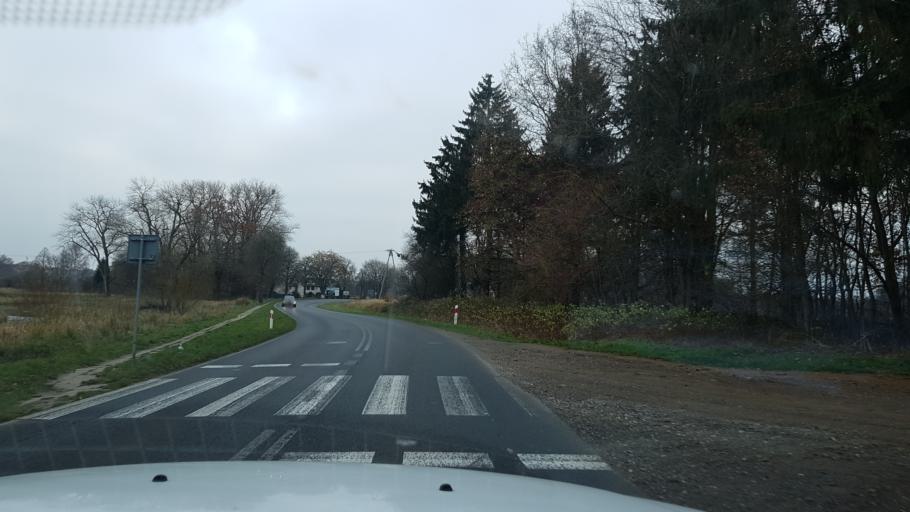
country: PL
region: West Pomeranian Voivodeship
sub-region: Powiat gryficki
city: Trzebiatow
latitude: 54.0666
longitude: 15.2508
